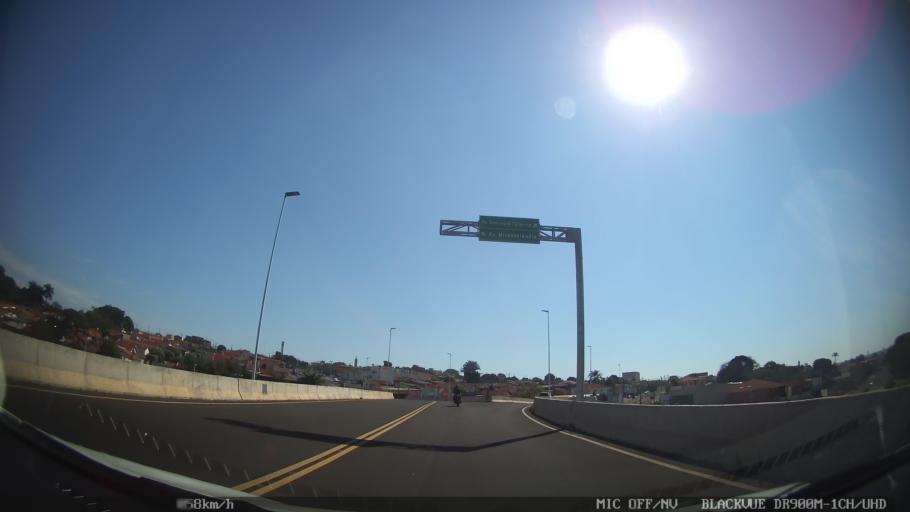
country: BR
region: Sao Paulo
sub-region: Sao Jose Do Rio Preto
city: Sao Jose do Rio Preto
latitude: -20.7887
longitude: -49.3889
